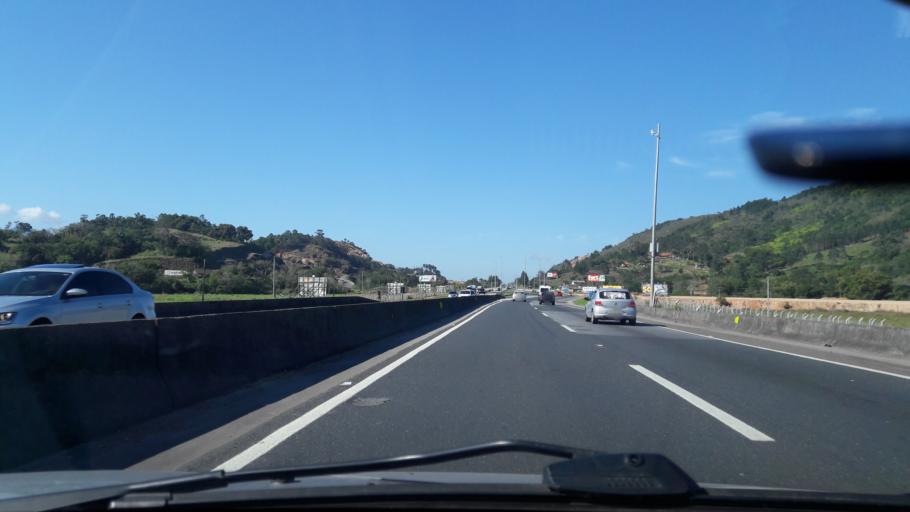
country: BR
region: Santa Catarina
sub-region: Tijucas
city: Tijucas
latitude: -27.2763
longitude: -48.6315
